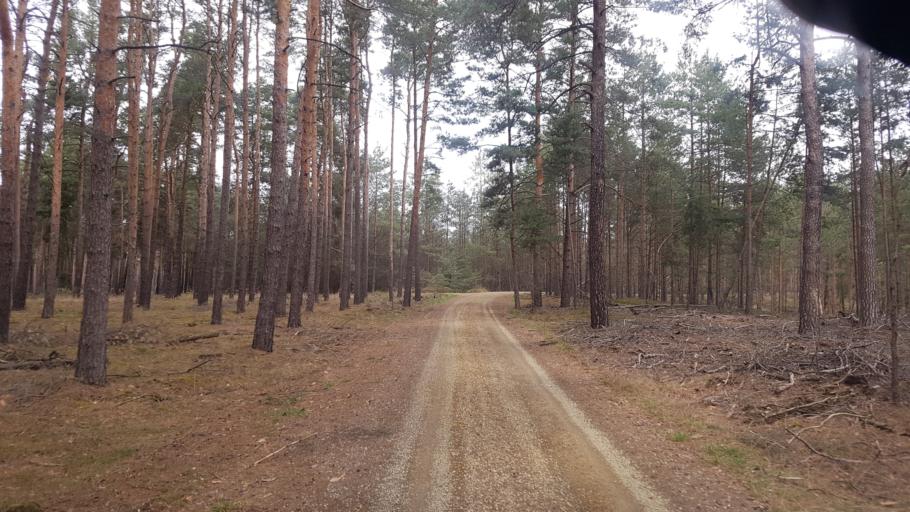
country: DE
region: Brandenburg
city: Schonborn
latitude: 51.6552
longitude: 13.4960
